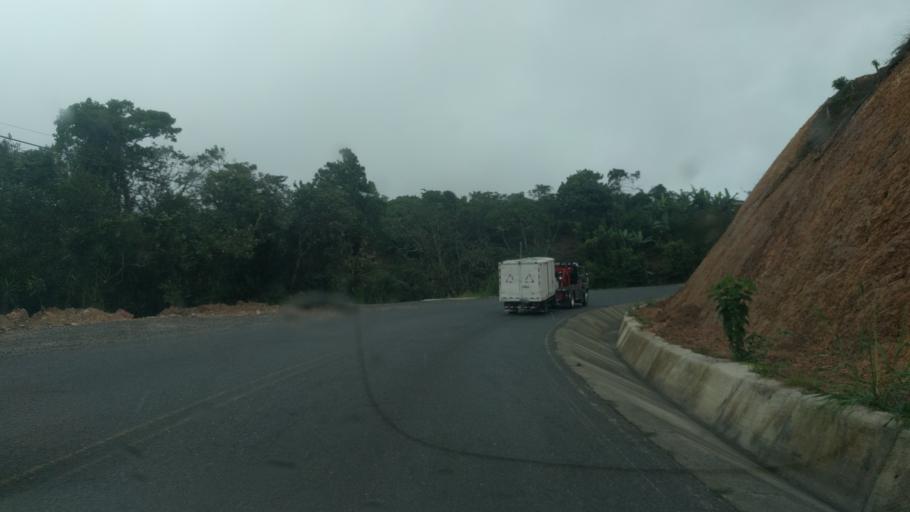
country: CR
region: Alajuela
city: San Rafael
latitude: 10.0341
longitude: -84.5133
